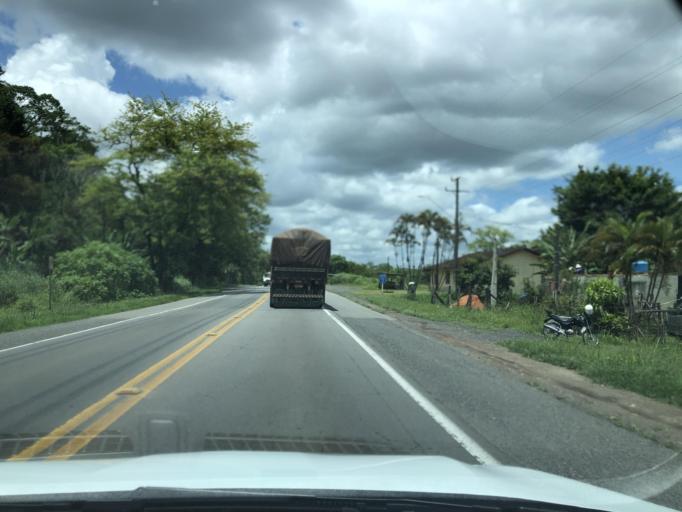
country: BR
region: Santa Catarina
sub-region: Sao Francisco Do Sul
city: Sao Francisco do Sul
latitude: -26.3633
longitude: -48.6639
